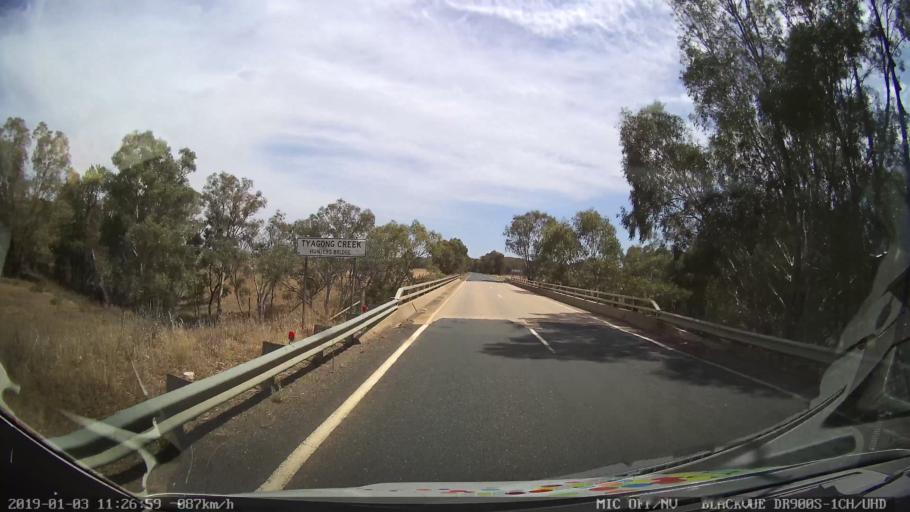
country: AU
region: New South Wales
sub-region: Weddin
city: Grenfell
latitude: -34.0179
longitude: 148.2217
